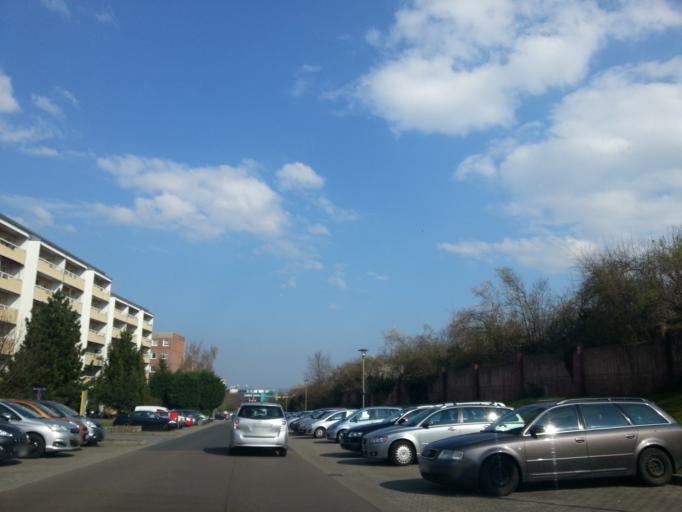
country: DE
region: Saxony
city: Freital
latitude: 51.0488
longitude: 13.6555
